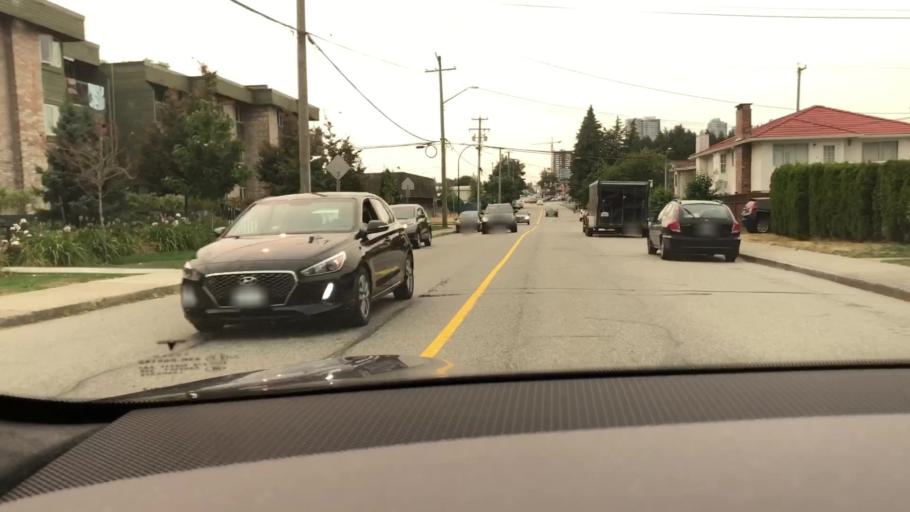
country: CA
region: British Columbia
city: Burnaby
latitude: 49.2218
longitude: -122.9748
